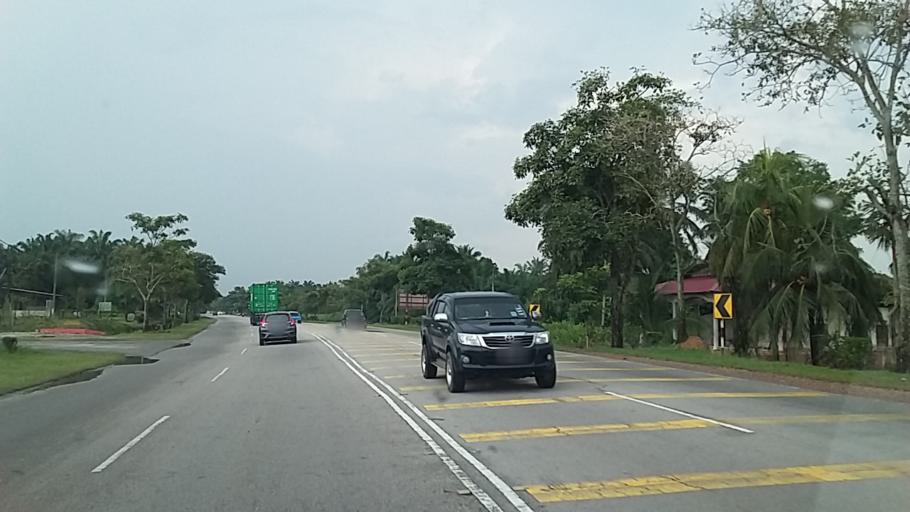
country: MY
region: Johor
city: Parit Raja
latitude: 1.8758
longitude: 103.1422
